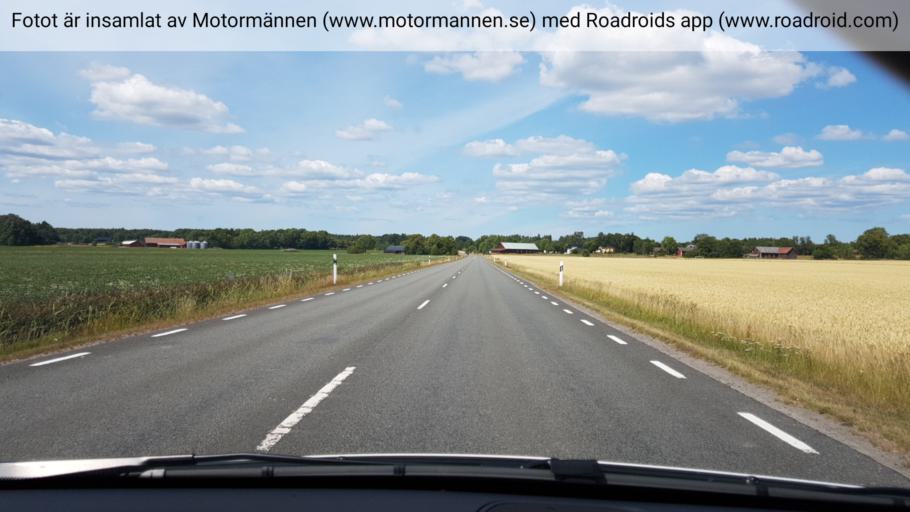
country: SE
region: Vaestra Goetaland
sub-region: Toreboda Kommun
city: Toereboda
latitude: 58.6101
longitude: 14.0052
